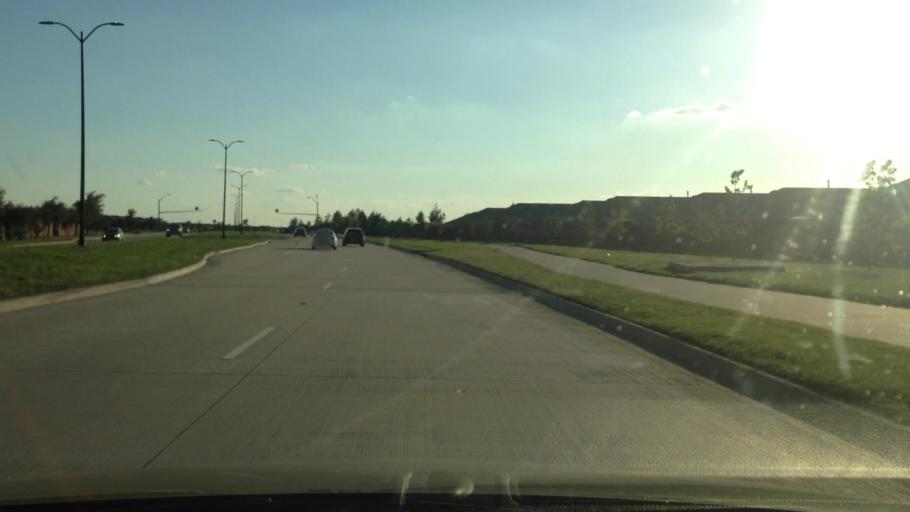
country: US
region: Texas
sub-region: Denton County
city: Little Elm
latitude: 33.1449
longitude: -96.9074
